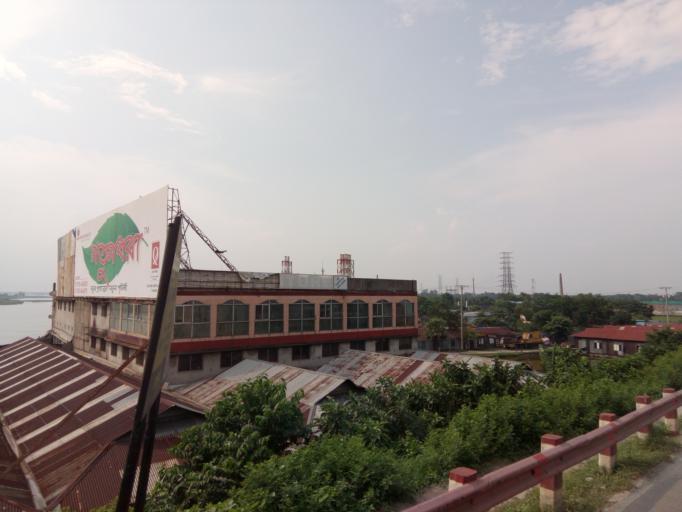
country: BD
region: Dhaka
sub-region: Dhaka
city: Dhaka
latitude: 23.6445
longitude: 90.3487
